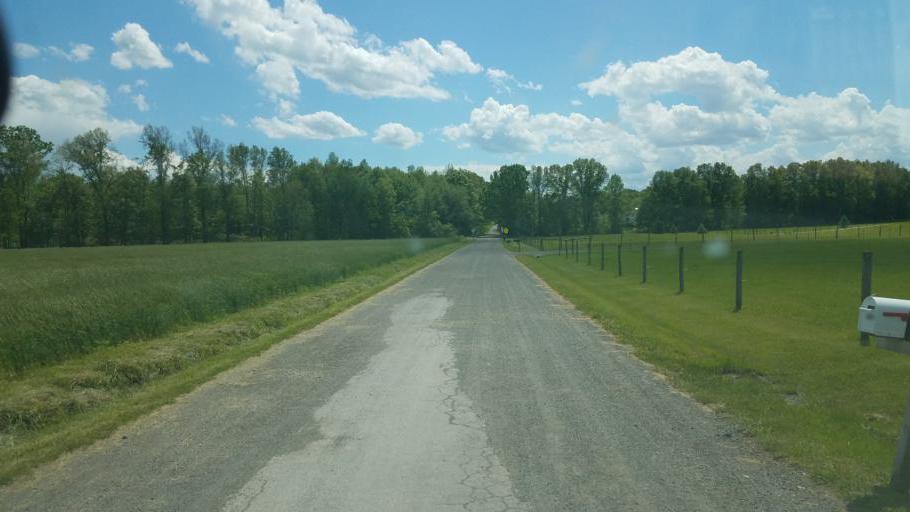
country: US
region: Ohio
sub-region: Geauga County
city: Middlefield
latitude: 41.3843
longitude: -80.9909
